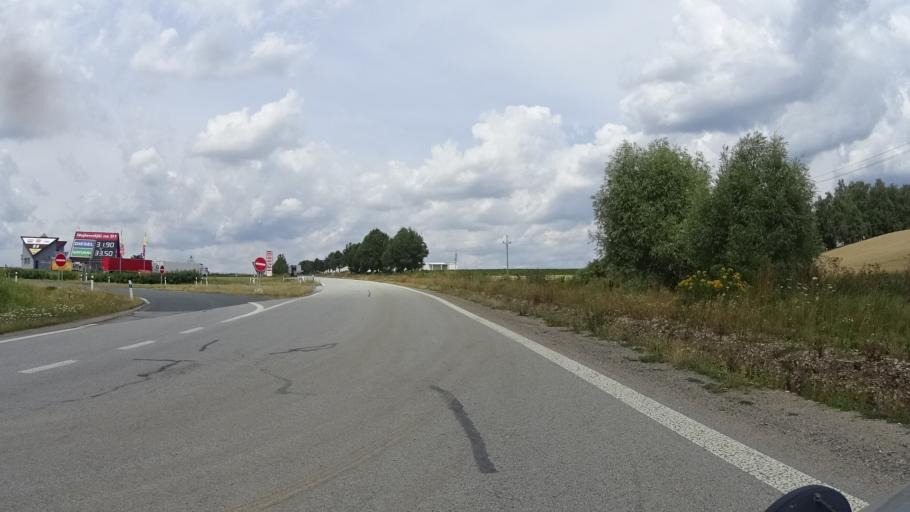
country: CZ
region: Vysocina
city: Merin
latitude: 49.3985
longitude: 15.8827
